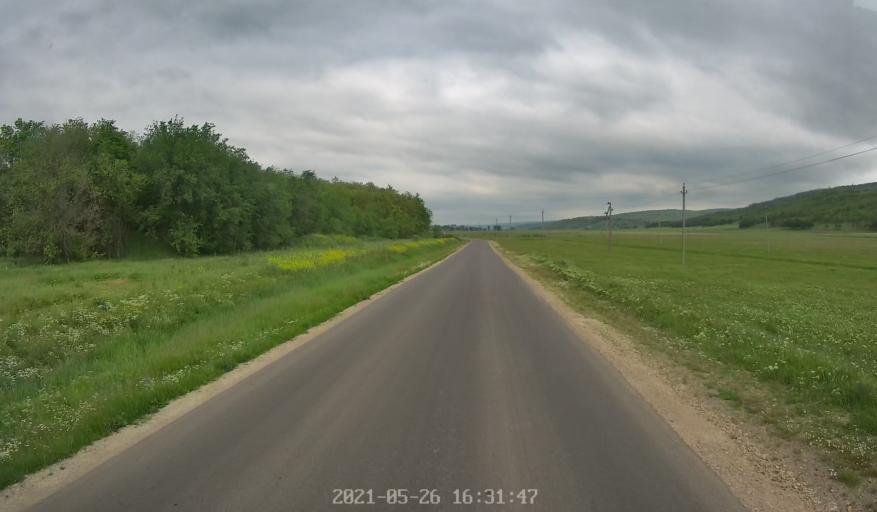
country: MD
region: Hincesti
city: Dancu
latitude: 46.8099
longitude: 28.3571
